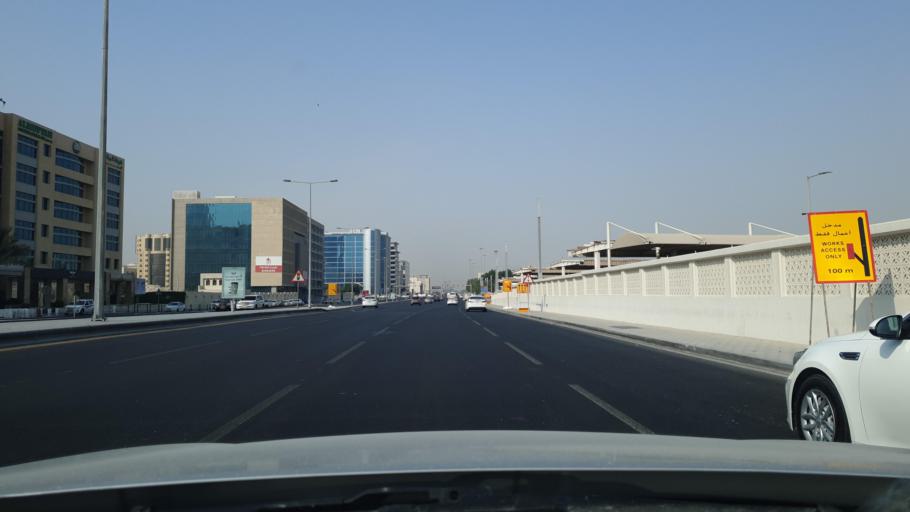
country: QA
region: Baladiyat ad Dawhah
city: Doha
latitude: 25.2900
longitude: 51.5114
